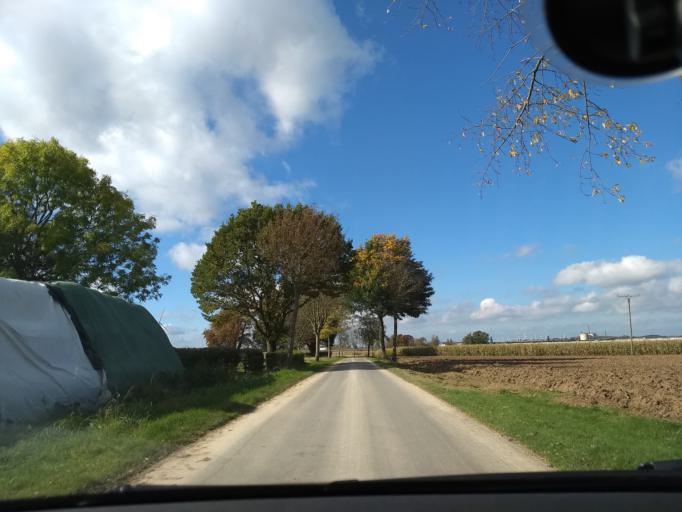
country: DE
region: North Rhine-Westphalia
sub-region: Regierungsbezirk Arnsberg
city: Ruthen
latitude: 51.5005
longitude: 8.4995
